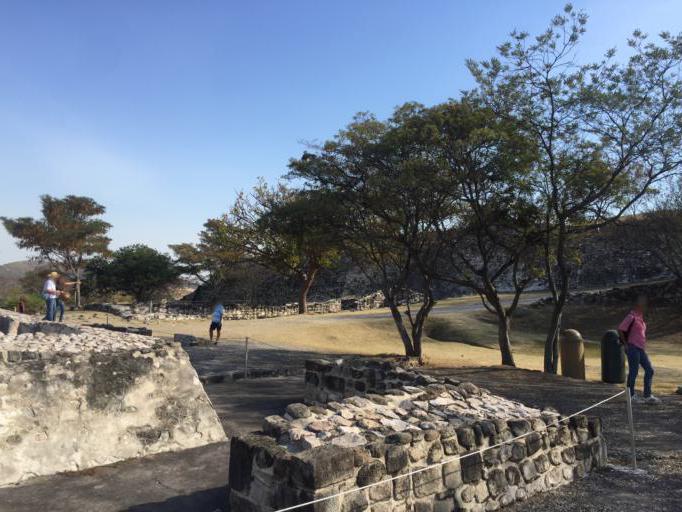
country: MX
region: Morelos
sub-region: Miacatlan
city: Xochicalco (Cirenio Longares)
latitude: 18.8055
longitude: -99.2966
